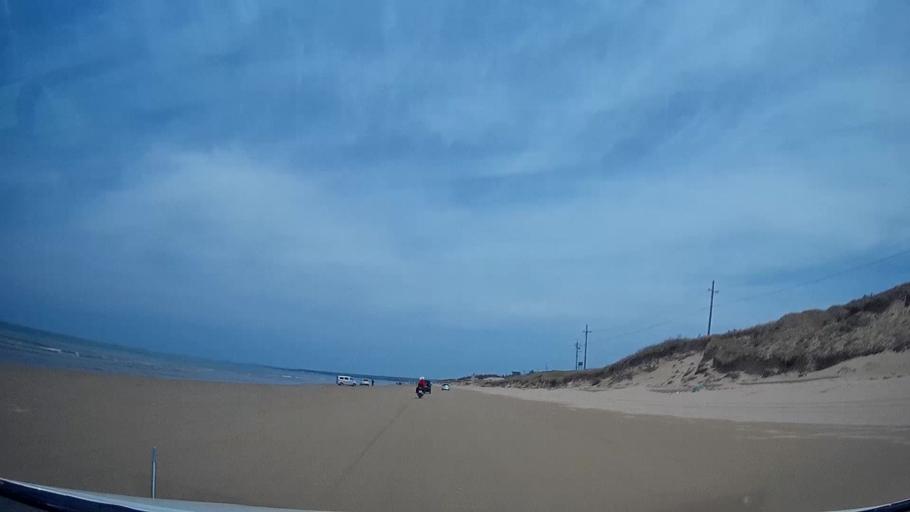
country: JP
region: Ishikawa
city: Hakui
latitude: 36.8541
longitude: 136.7544
